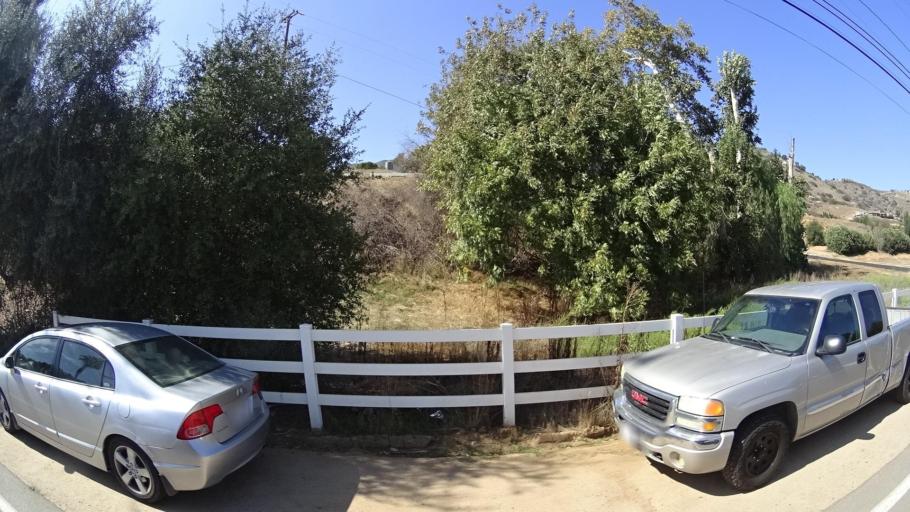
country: US
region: California
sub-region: San Diego County
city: Crest
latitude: 32.7922
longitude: -116.8458
